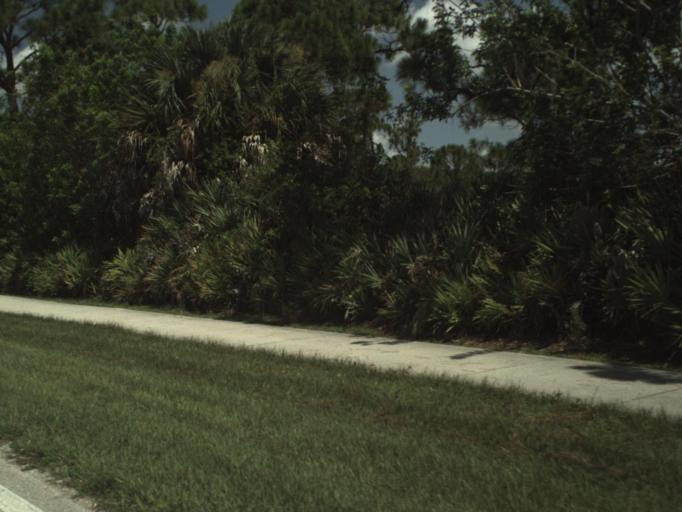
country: US
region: Florida
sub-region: Martin County
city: Jensen Beach
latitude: 27.2454
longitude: -80.2570
